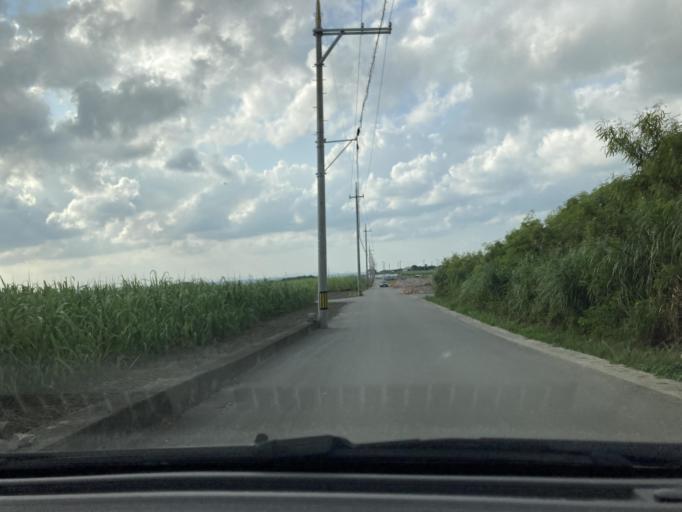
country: JP
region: Okinawa
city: Itoman
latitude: 26.0820
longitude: 127.6693
